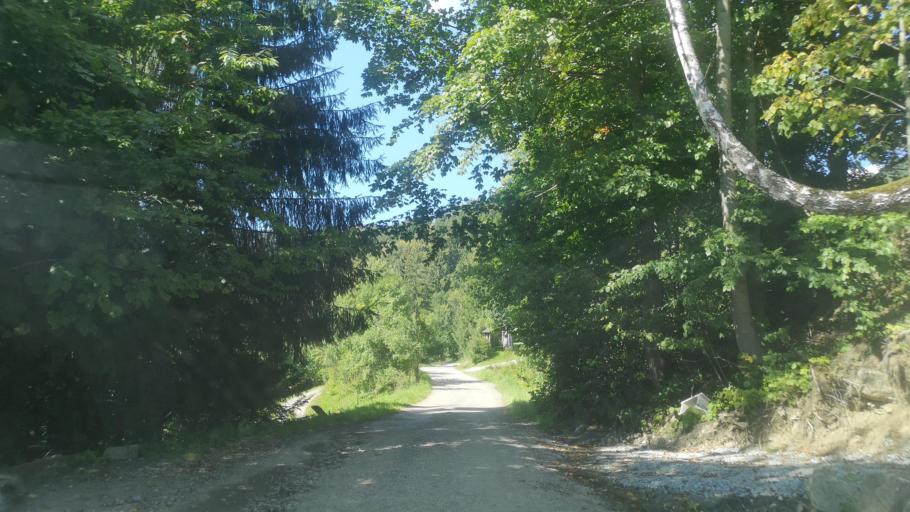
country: SK
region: Zilinsky
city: Oravska Lesna
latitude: 49.2939
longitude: 19.1399
